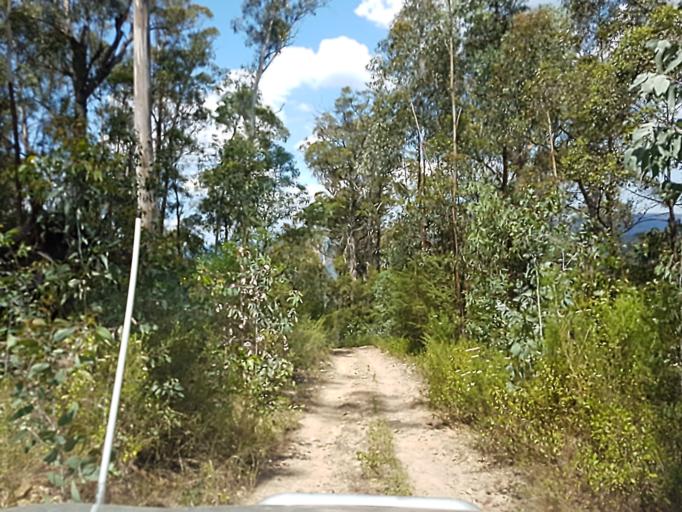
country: AU
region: Victoria
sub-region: East Gippsland
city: Lakes Entrance
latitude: -37.4036
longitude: 148.2991
